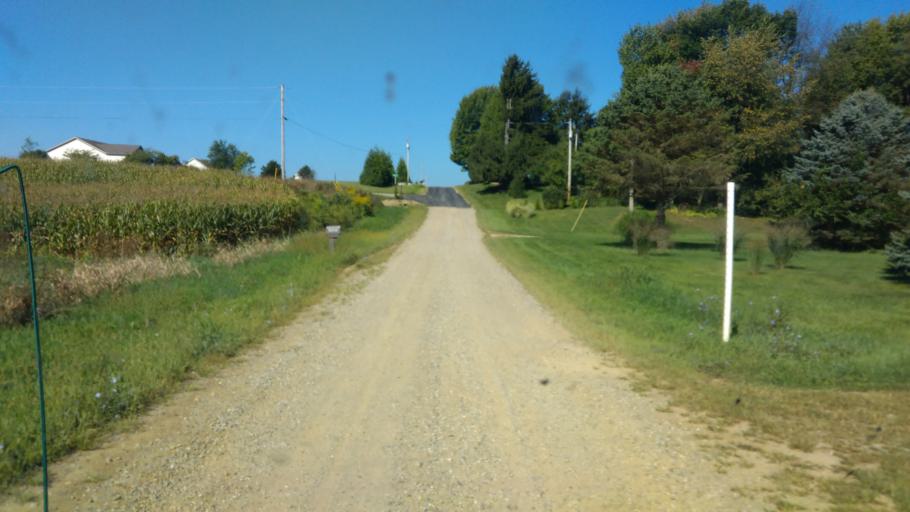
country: US
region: Ohio
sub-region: Knox County
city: Fredericktown
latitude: 40.4884
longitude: -82.4470
